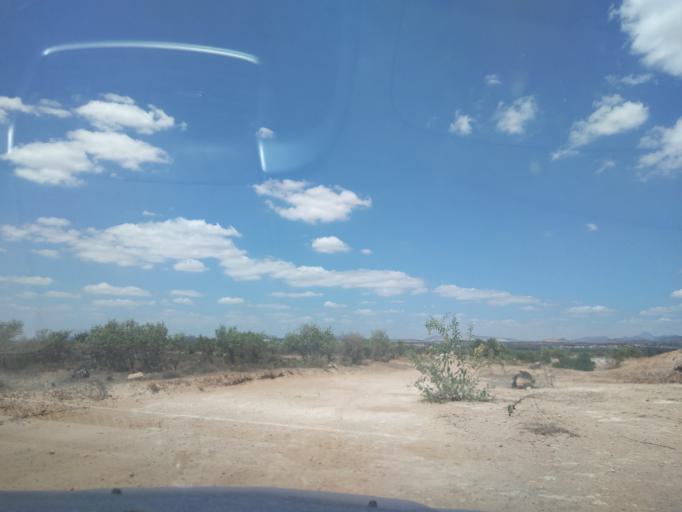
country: TN
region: Susah
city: Harqalah
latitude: 36.1658
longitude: 10.4442
